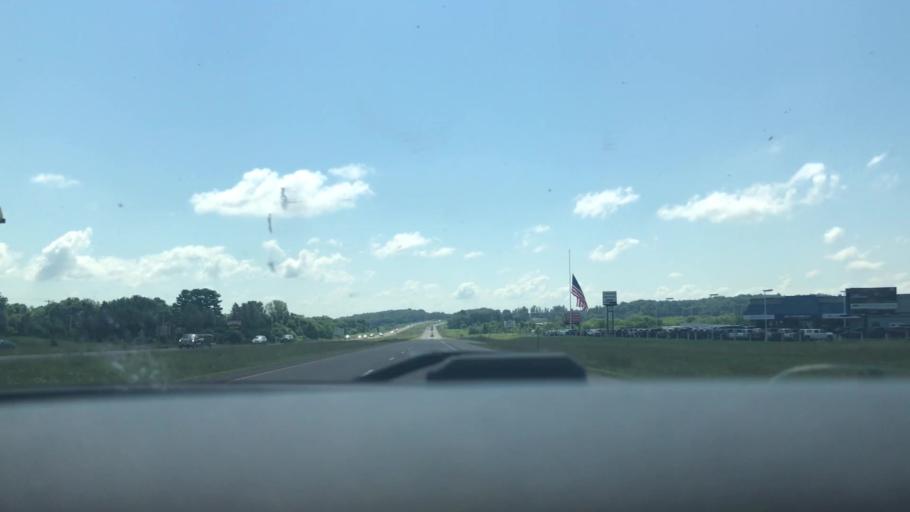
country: US
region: Wisconsin
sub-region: Chippewa County
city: Bloomer
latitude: 45.0985
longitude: -91.5029
